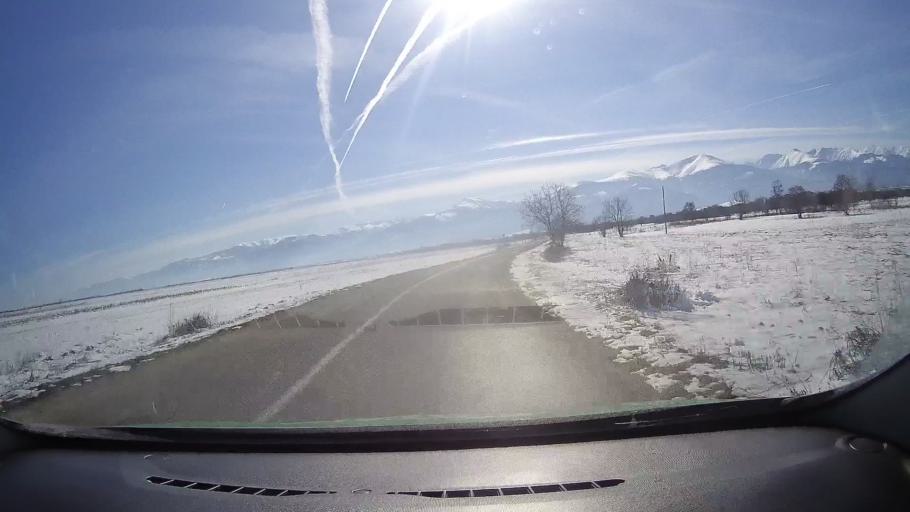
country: RO
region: Brasov
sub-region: Comuna Sambata de Sus
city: Sambata de Sus
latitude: 45.7458
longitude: 24.8428
